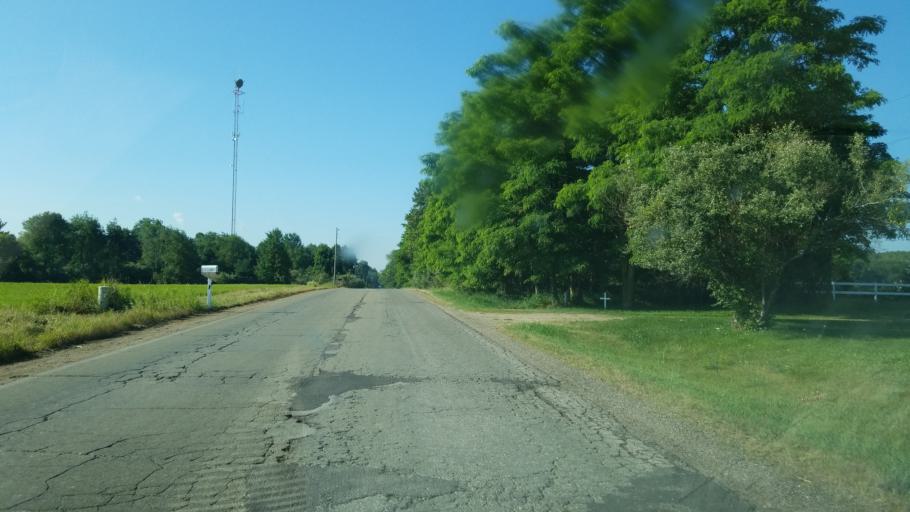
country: US
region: Michigan
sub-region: Mecosta County
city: Canadian Lakes
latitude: 43.5271
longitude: -85.3923
